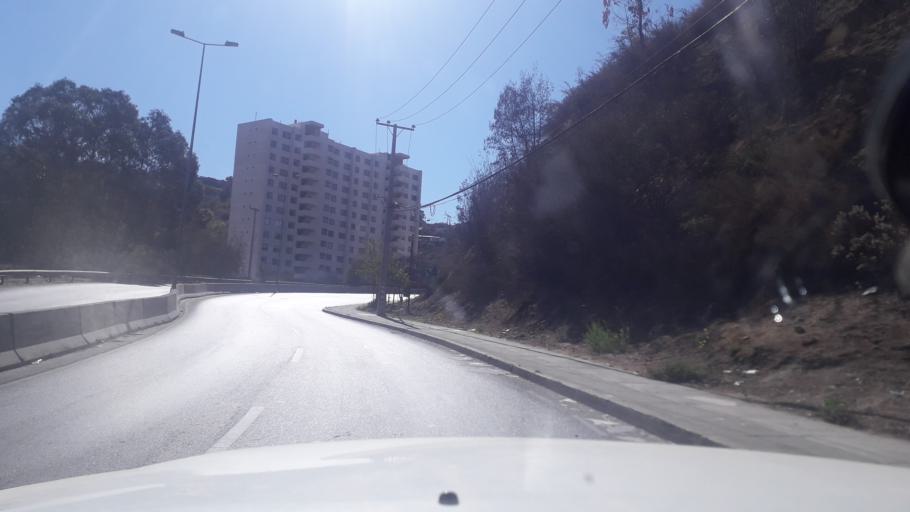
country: CL
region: Valparaiso
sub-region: Provincia de Valparaiso
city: Vina del Mar
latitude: -33.0363
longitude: -71.5161
